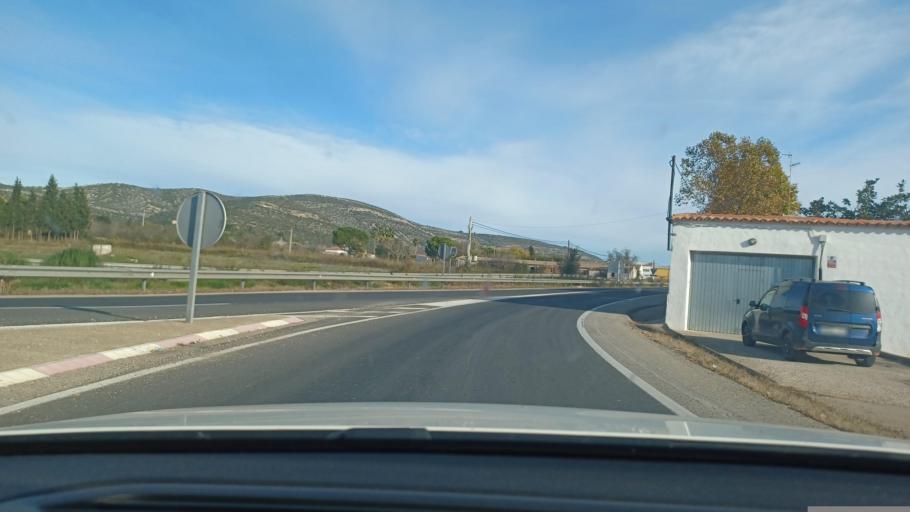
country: ES
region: Catalonia
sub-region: Provincia de Tarragona
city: Ulldecona
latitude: 40.6031
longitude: 0.4545
